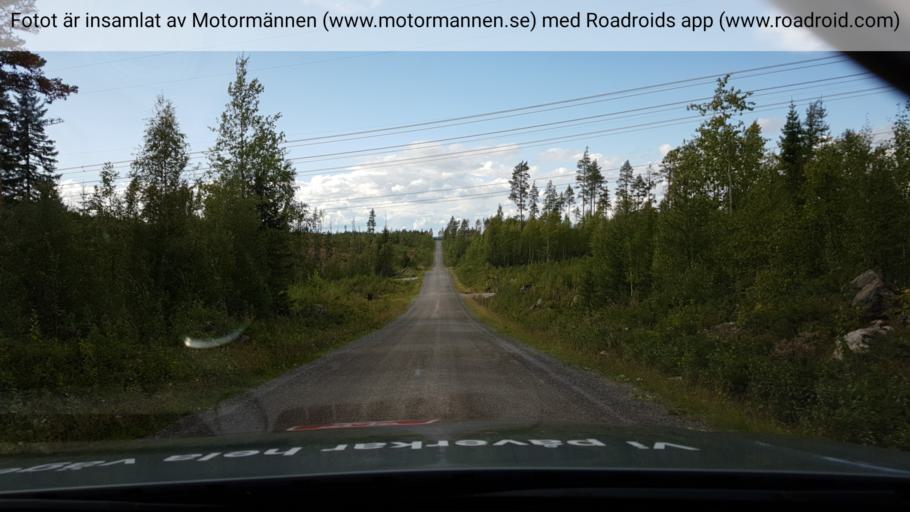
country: SE
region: Jaemtland
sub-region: OEstersunds Kommun
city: Lit
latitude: 63.2909
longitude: 15.3488
